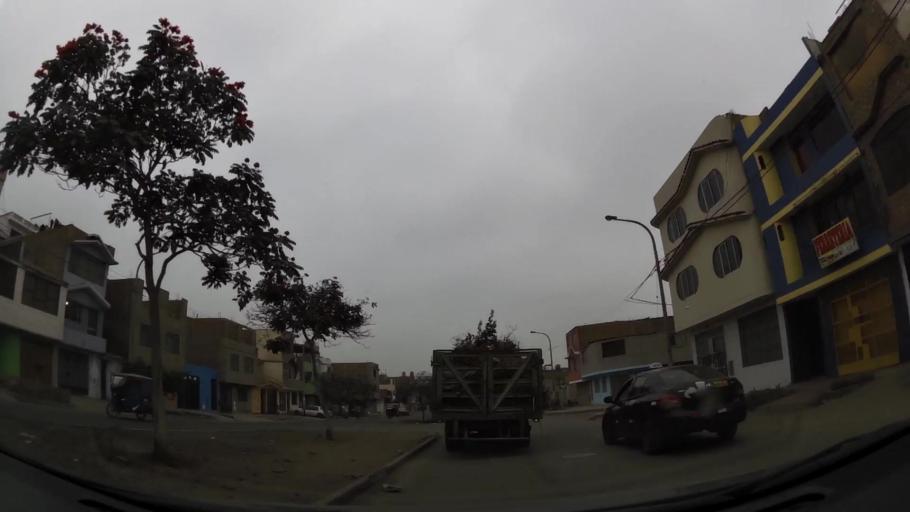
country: PE
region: Lima
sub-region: Lima
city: Urb. Santo Domingo
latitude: -11.9159
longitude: -77.0511
